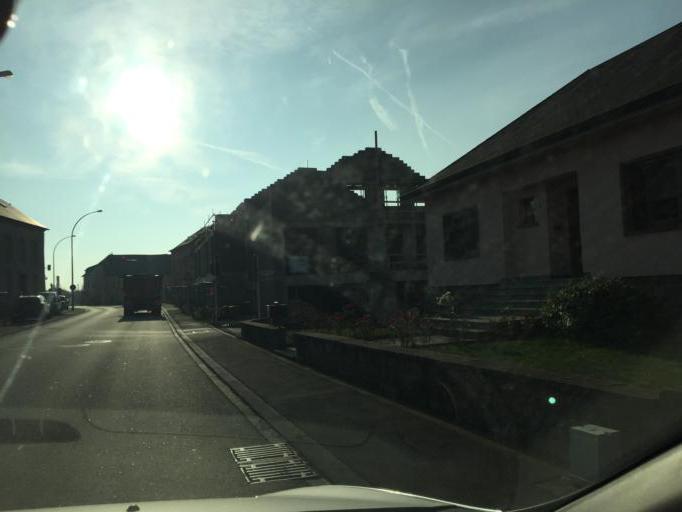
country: LU
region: Grevenmacher
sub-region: Canton de Remich
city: Dalheim
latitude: 49.5347
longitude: 6.2462
